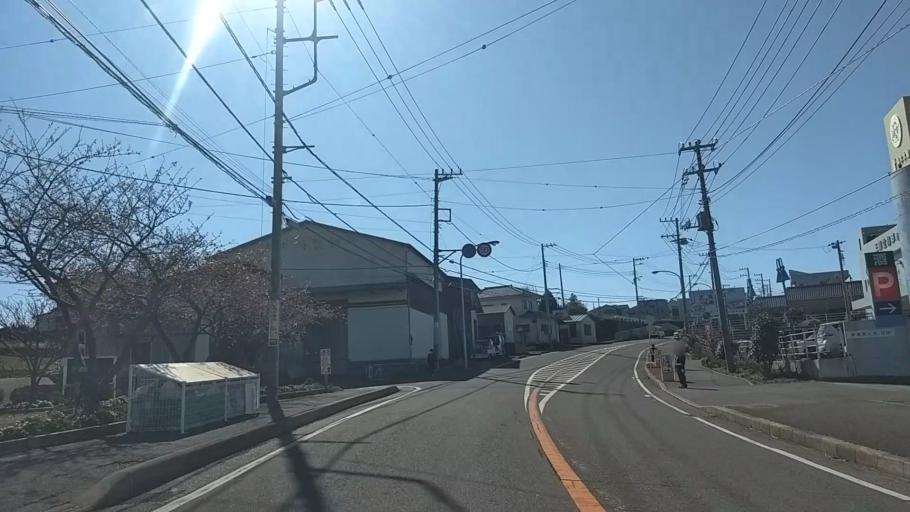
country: JP
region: Kanagawa
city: Miura
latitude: 35.1720
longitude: 139.6429
